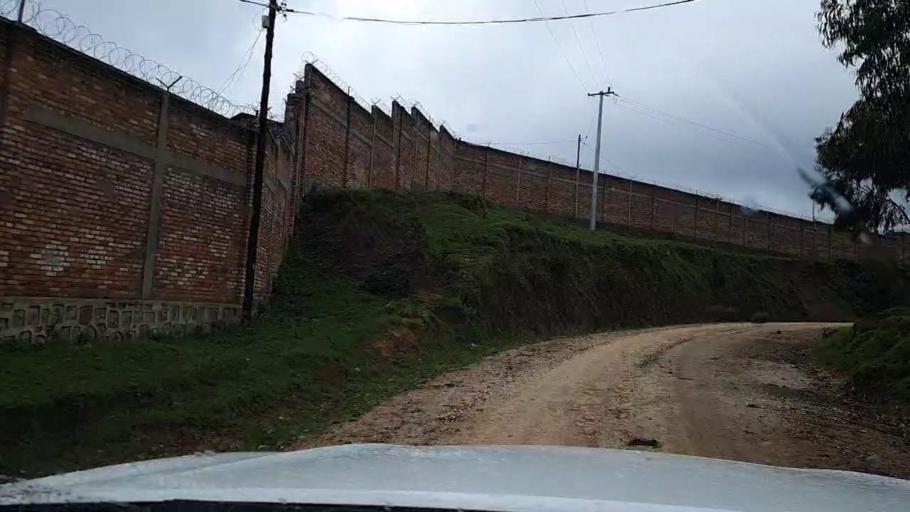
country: RW
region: Southern Province
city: Nzega
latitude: -2.3687
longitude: 29.3809
